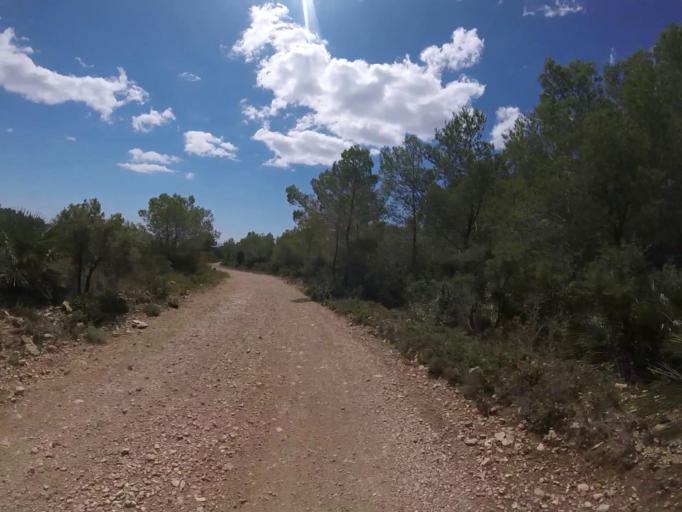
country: ES
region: Valencia
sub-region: Provincia de Castello
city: Alcoceber
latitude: 40.2884
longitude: 0.3182
